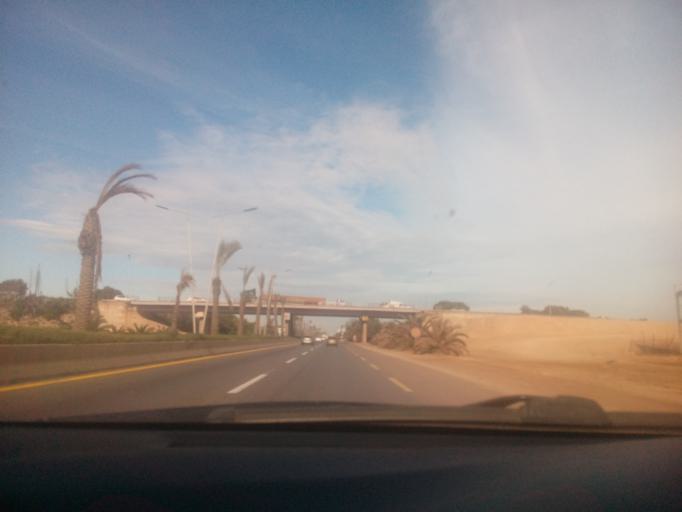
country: DZ
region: Oran
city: Es Senia
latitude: 35.6242
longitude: -0.5856
